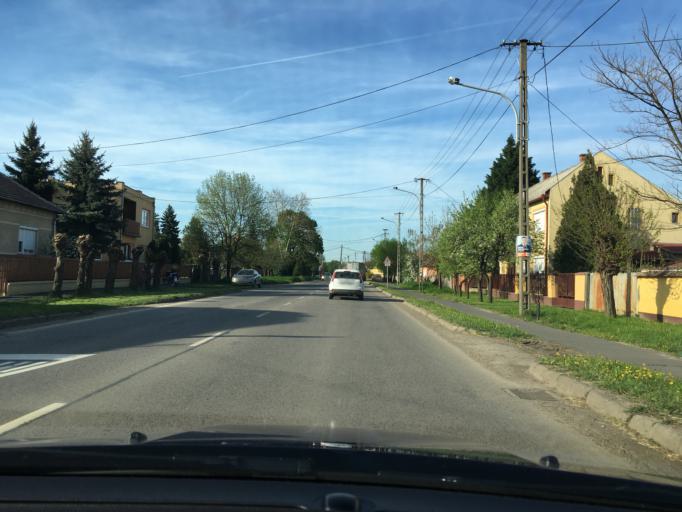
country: HU
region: Bekes
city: Korosladany
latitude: 46.9615
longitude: 21.0848
